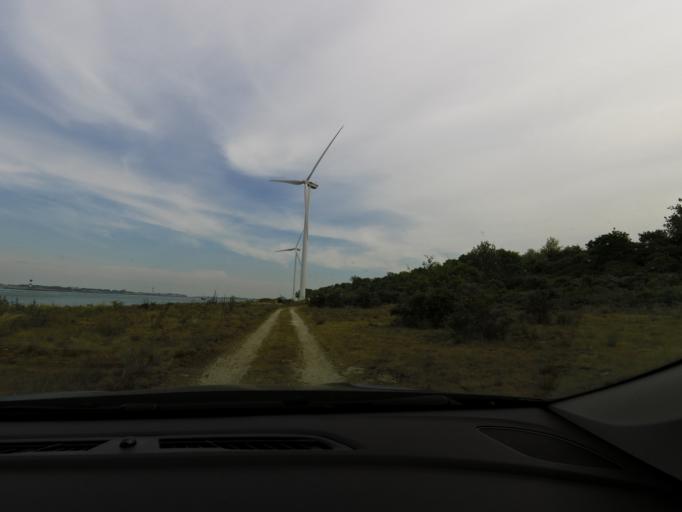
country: NL
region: South Holland
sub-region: Gemeente Rotterdam
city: Hoek van Holland
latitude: 51.9792
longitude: 4.0620
